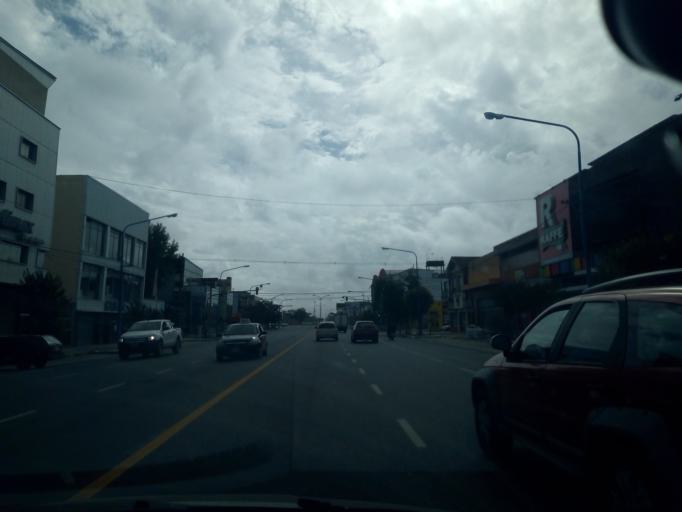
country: AR
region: Buenos Aires
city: Mar del Plata
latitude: -37.9816
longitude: -57.5796
